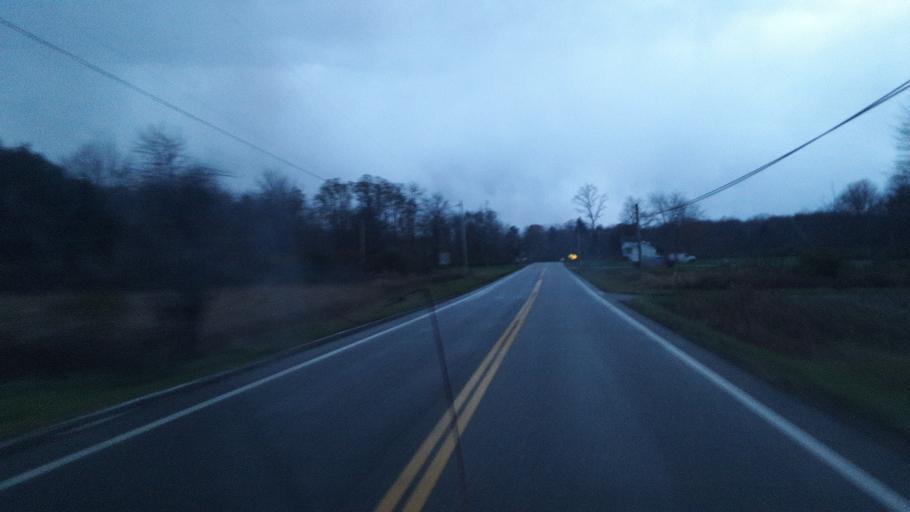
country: US
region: Ohio
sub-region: Portage County
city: Mantua
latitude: 41.3508
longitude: -81.2237
